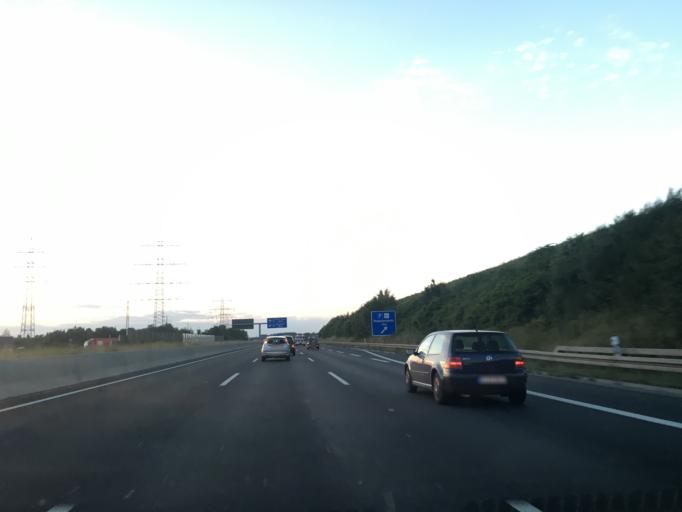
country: DE
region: North Rhine-Westphalia
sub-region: Regierungsbezirk Dusseldorf
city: Neuss
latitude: 51.2046
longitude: 6.6505
